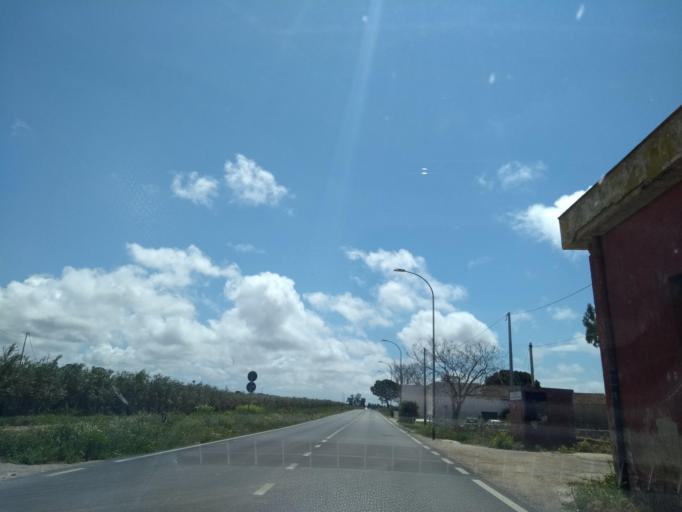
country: IT
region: Sicily
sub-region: Trapani
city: Rilievo
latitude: 37.9039
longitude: 12.5312
